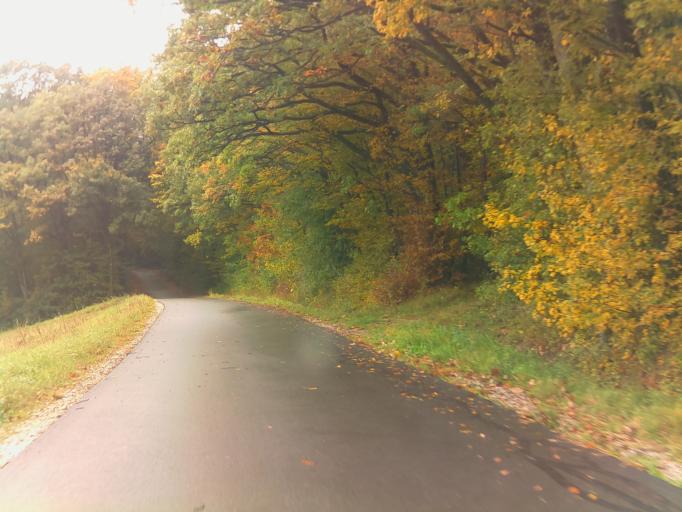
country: DE
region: Bavaria
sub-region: Upper Franconia
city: Schesslitz
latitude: 50.0191
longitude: 11.0170
